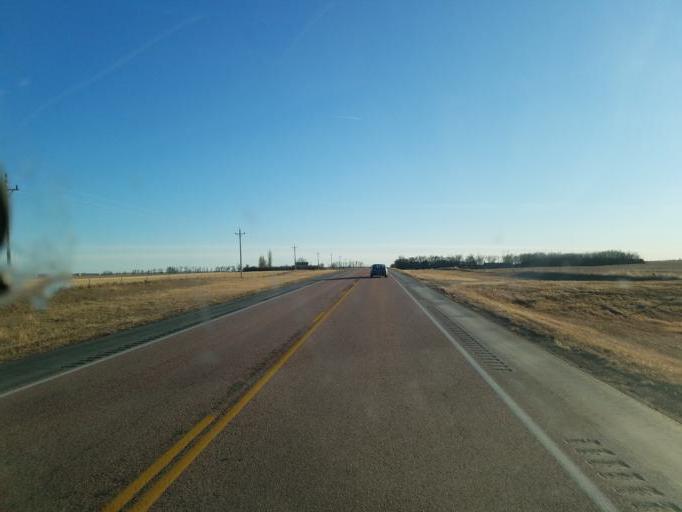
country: US
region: South Dakota
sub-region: Bon Homme County
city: Tyndall
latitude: 43.1620
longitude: -97.9710
